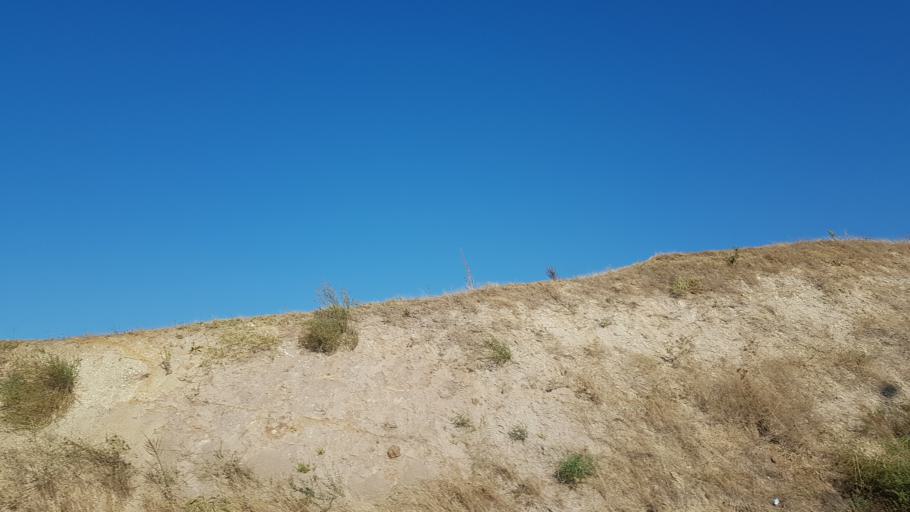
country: TR
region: Balikesir
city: Ertugrul
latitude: 39.6292
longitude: 27.7065
